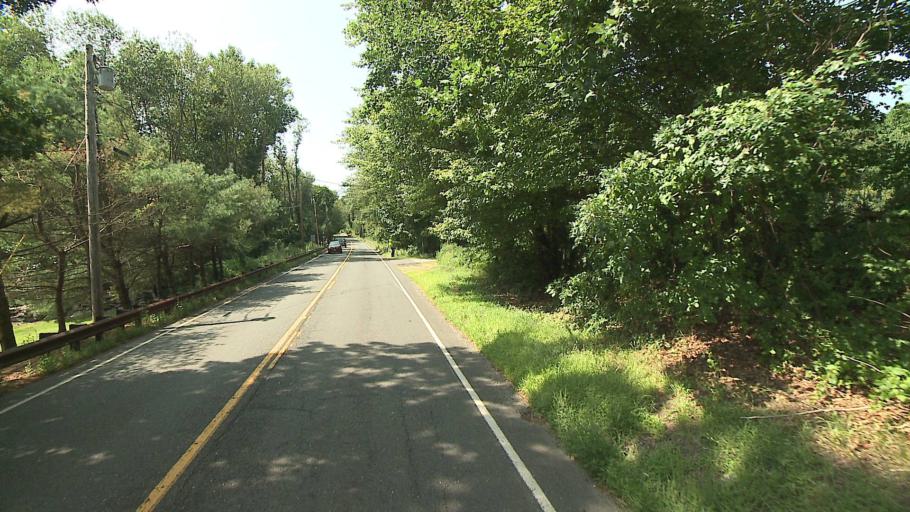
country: US
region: Connecticut
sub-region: Fairfield County
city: Shelton
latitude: 41.3348
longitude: -73.1794
